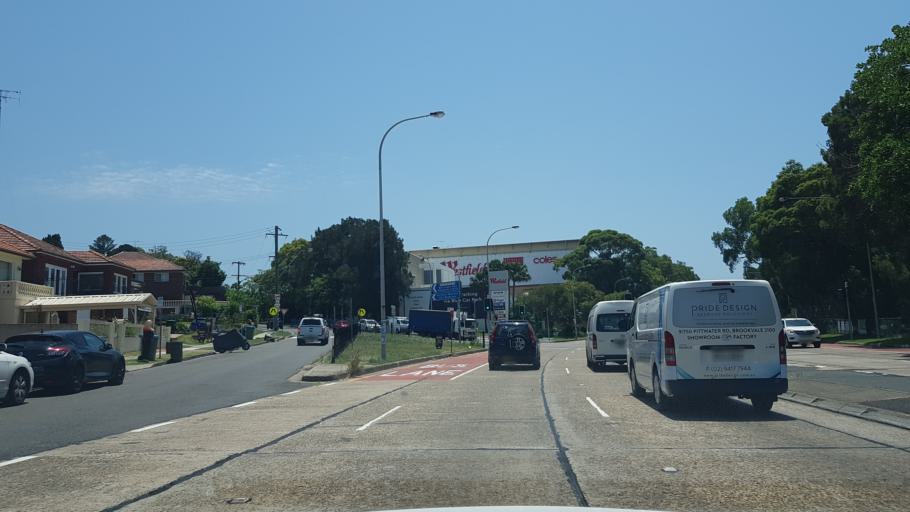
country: AU
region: New South Wales
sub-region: Warringah
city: North Manly
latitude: -33.7710
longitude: 151.2658
